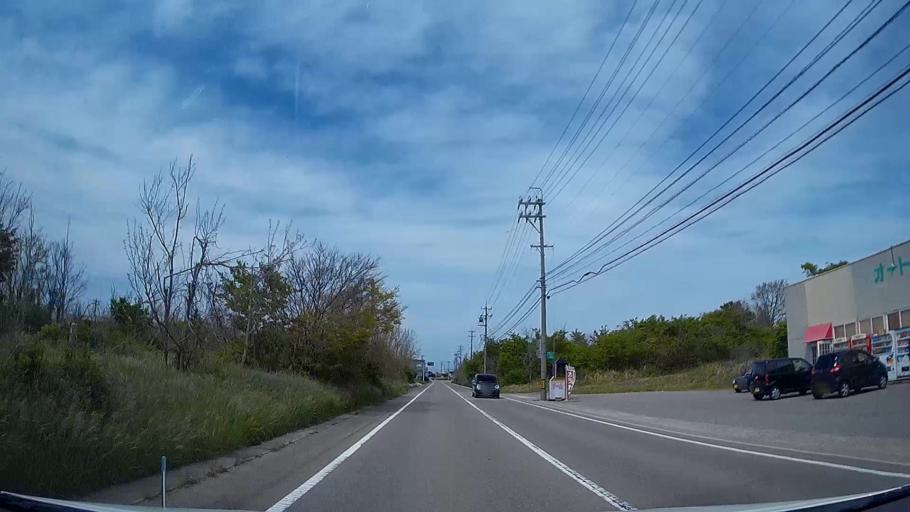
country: JP
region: Ishikawa
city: Hakui
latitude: 36.9758
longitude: 136.7757
